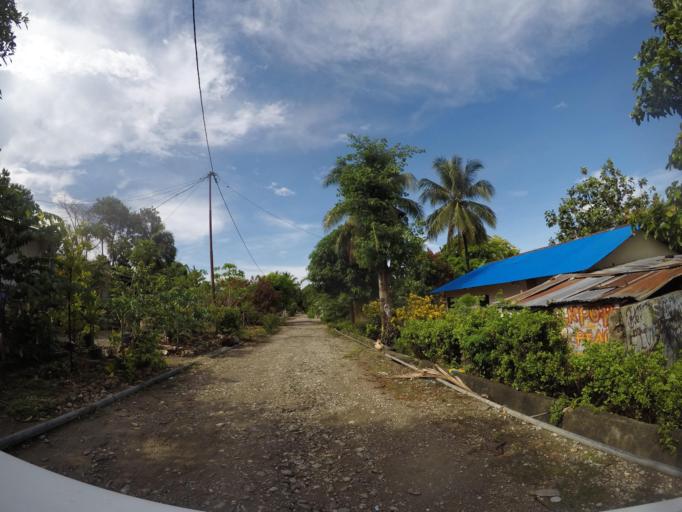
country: TL
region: Baucau
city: Baucau
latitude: -8.4800
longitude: 126.4576
